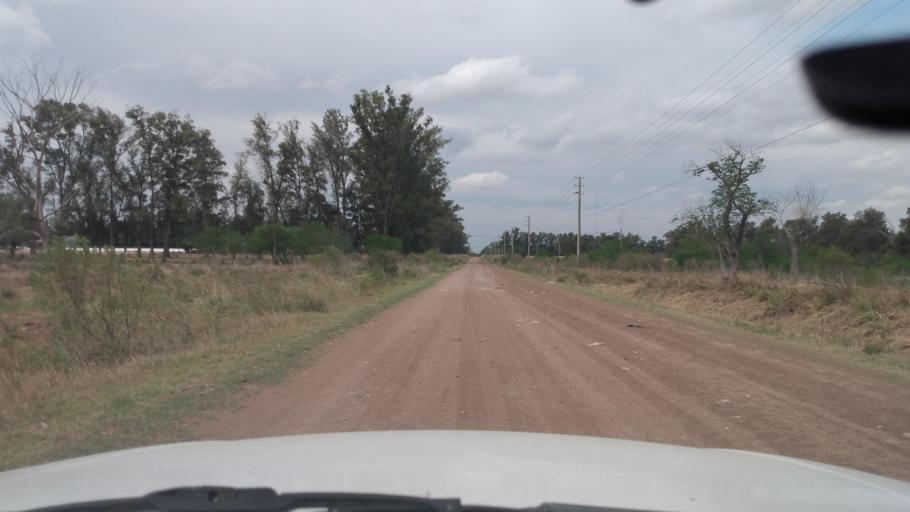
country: AR
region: Buenos Aires
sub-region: Partido de Lujan
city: Lujan
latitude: -34.5557
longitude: -59.1784
